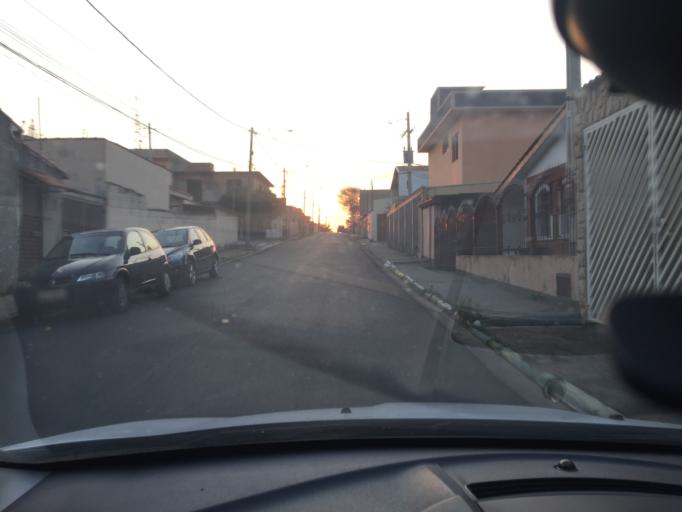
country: BR
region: Sao Paulo
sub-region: Varzea Paulista
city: Varzea Paulista
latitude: -23.2069
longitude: -46.8445
